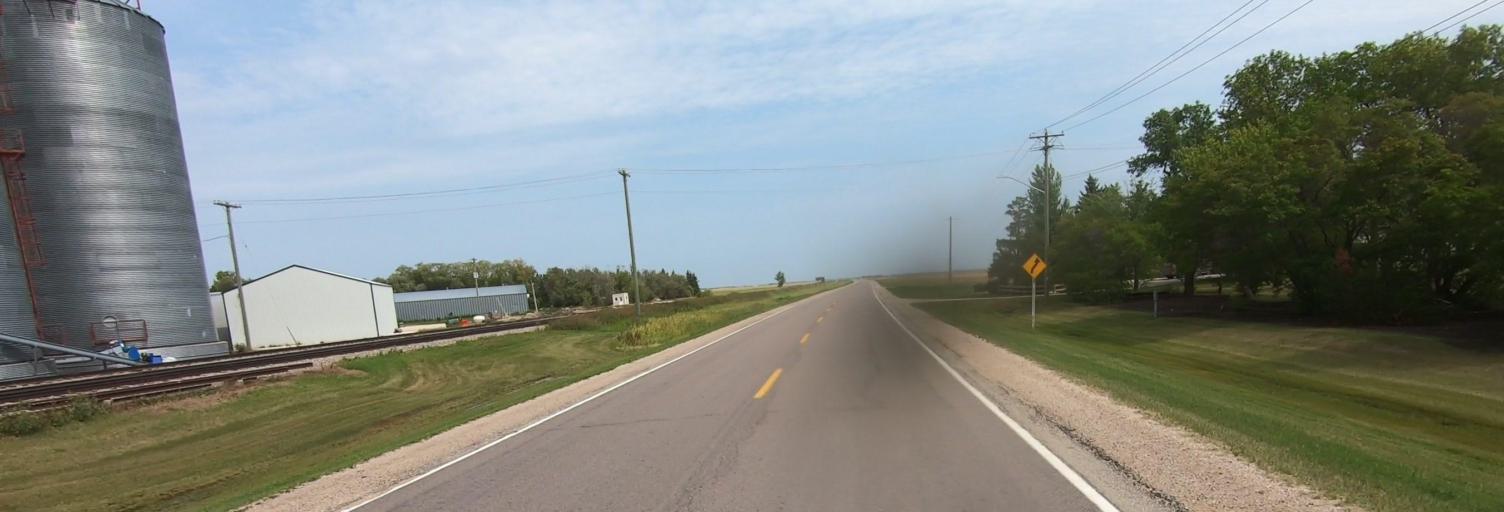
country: CA
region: Manitoba
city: Morris
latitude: 49.6146
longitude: -97.3210
